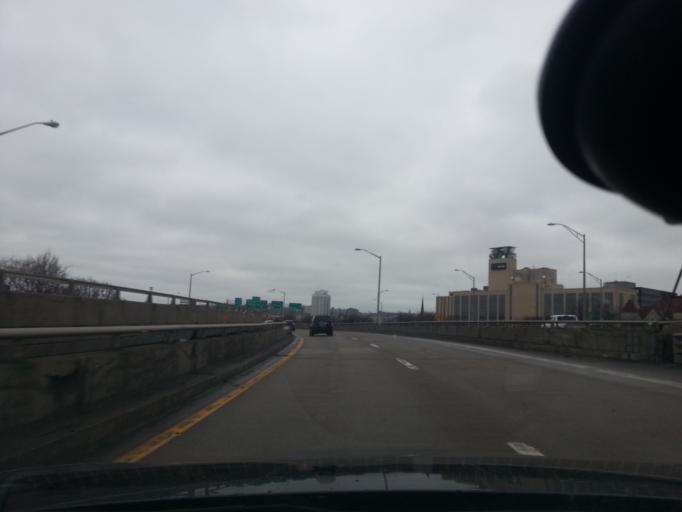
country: US
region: New York
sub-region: Onondaga County
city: Syracuse
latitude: 43.0522
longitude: -76.1501
